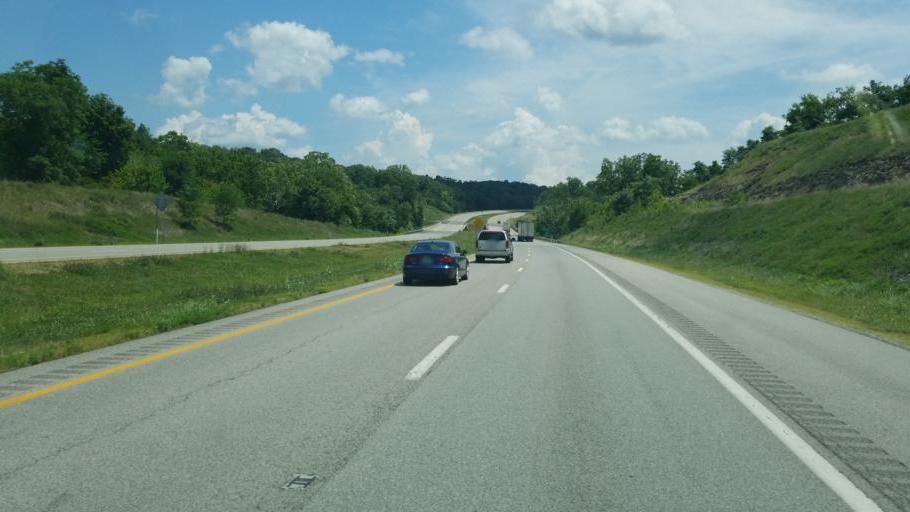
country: US
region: West Virginia
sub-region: Mason County
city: Point Pleasant
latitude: 38.7799
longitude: -82.0678
